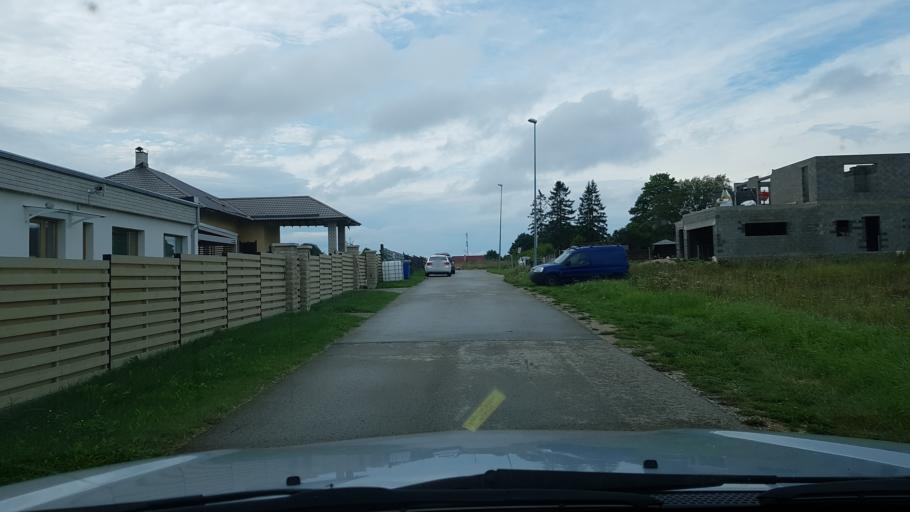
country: EE
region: Harju
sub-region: Joelaehtme vald
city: Loo
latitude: 59.4067
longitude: 24.9616
